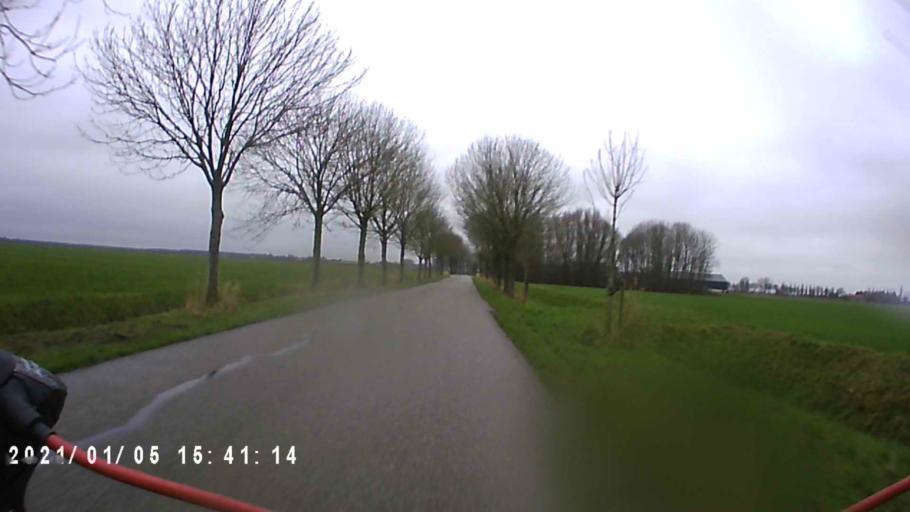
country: NL
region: Groningen
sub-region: Gemeente  Oldambt
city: Winschoten
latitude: 53.2090
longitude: 7.1389
